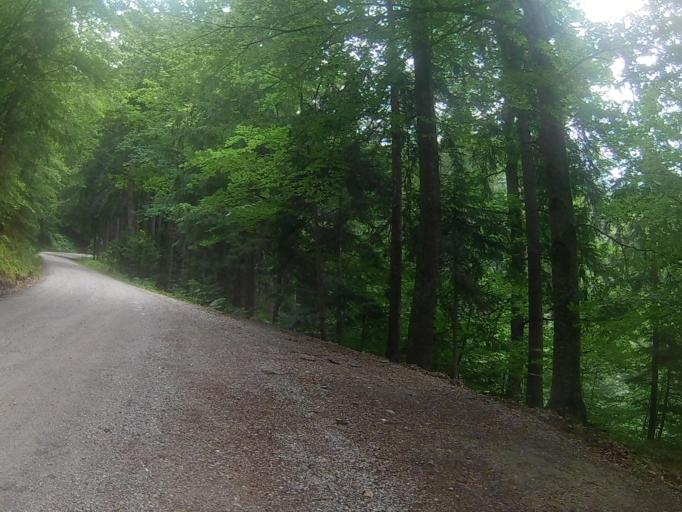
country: SI
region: Ruse
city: Ruse
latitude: 46.5252
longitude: 15.5366
